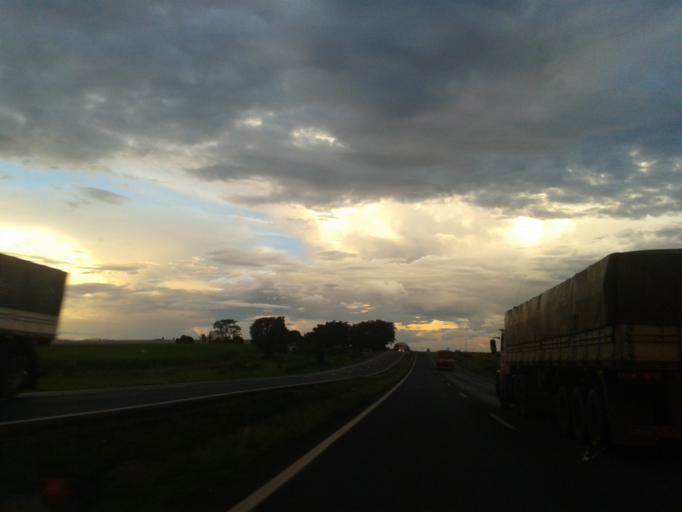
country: BR
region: Minas Gerais
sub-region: Centralina
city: Centralina
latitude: -18.7252
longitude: -49.1178
